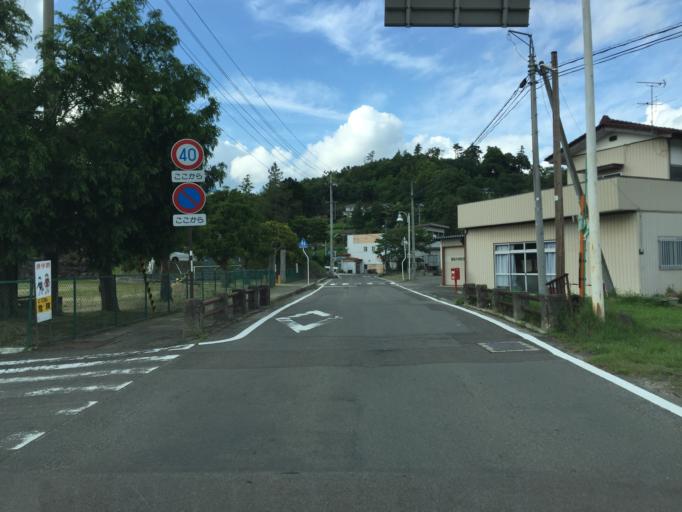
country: JP
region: Fukushima
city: Fukushima-shi
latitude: 37.6645
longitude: 140.5484
